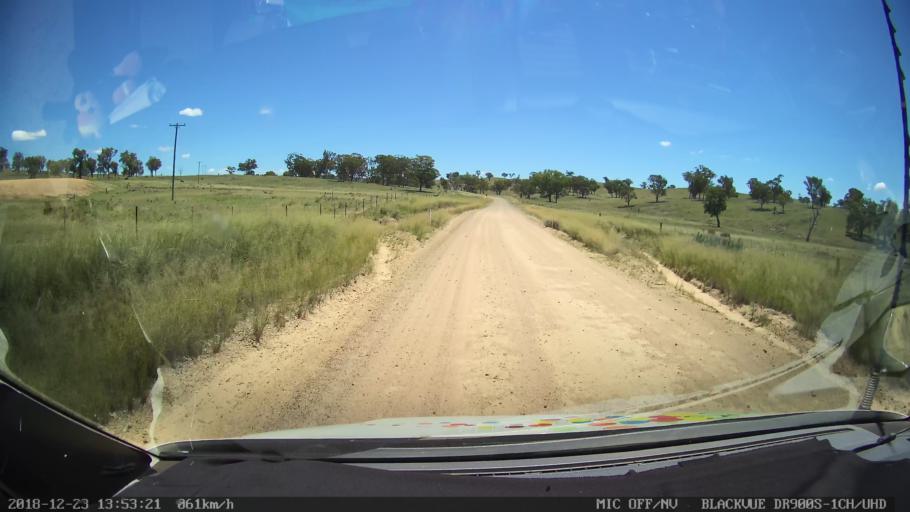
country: AU
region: New South Wales
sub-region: Tamworth Municipality
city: Manilla
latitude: -30.5524
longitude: 151.0955
